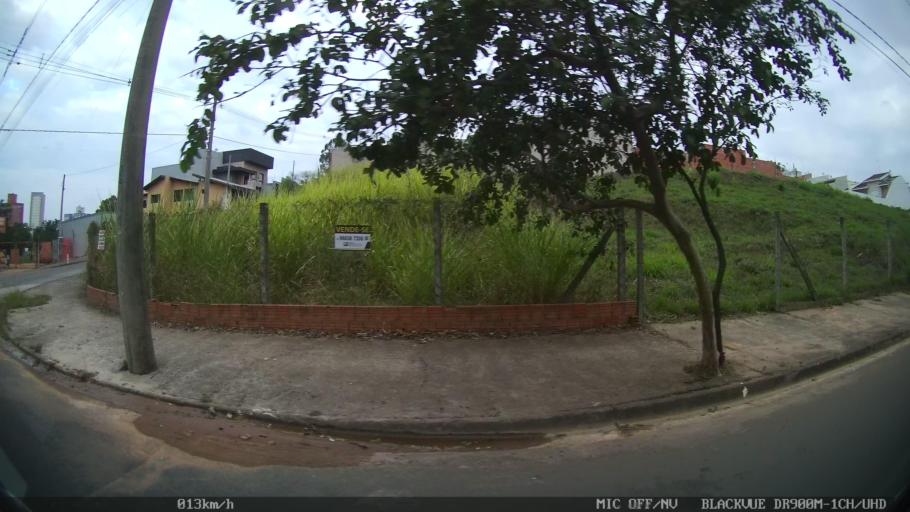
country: BR
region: Sao Paulo
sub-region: Americana
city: Americana
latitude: -22.7352
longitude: -47.3428
